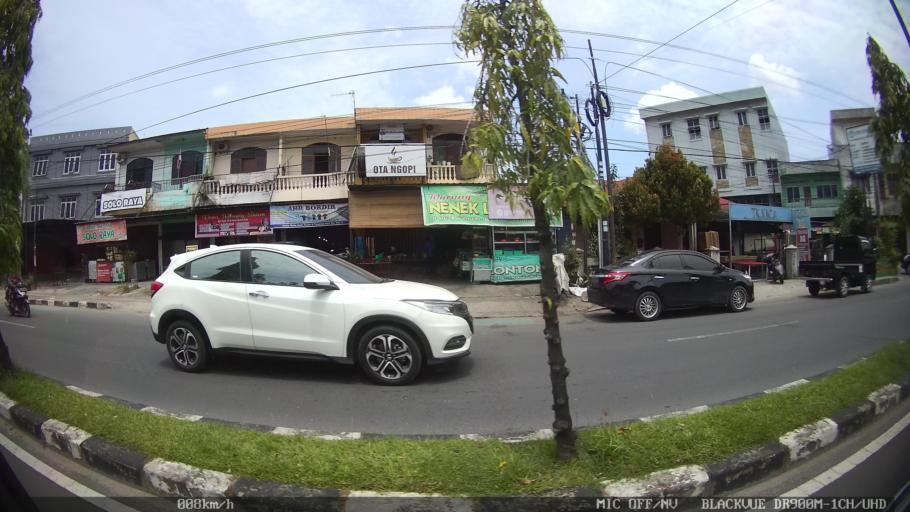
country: ID
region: North Sumatra
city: Sunggal
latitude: 3.5552
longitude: 98.6327
